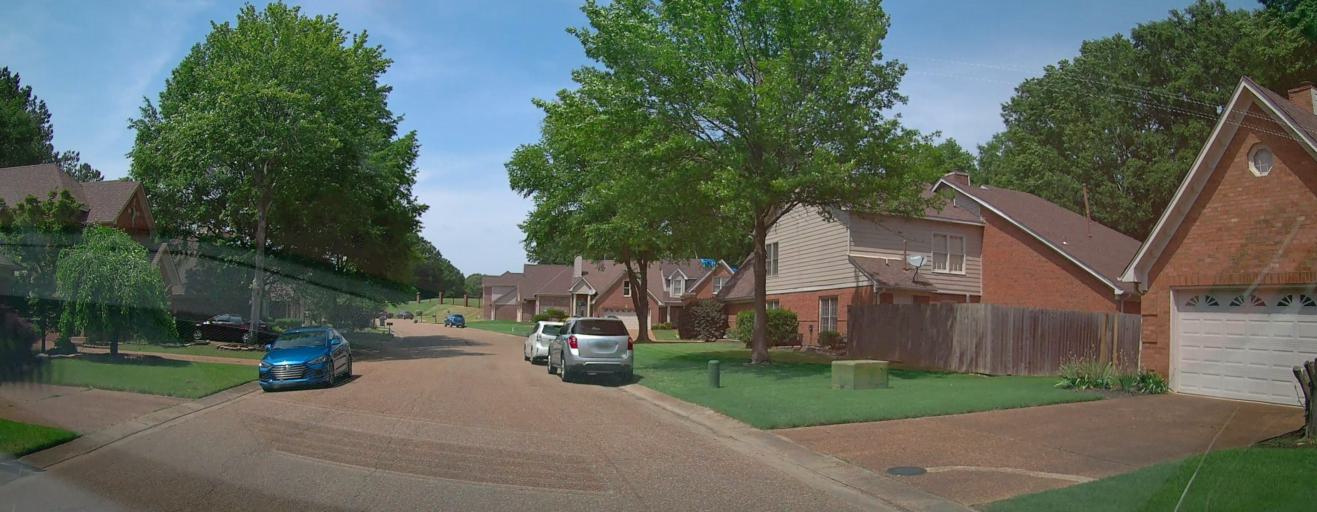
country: US
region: Tennessee
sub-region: Shelby County
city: Germantown
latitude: 35.0405
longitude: -89.7864
